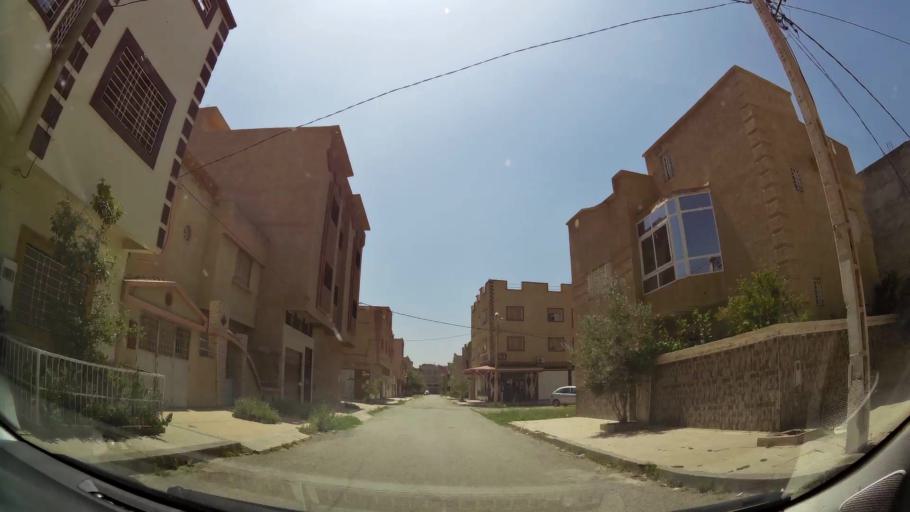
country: MA
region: Oriental
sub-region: Oujda-Angad
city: Oujda
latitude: 34.6943
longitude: -1.8827
